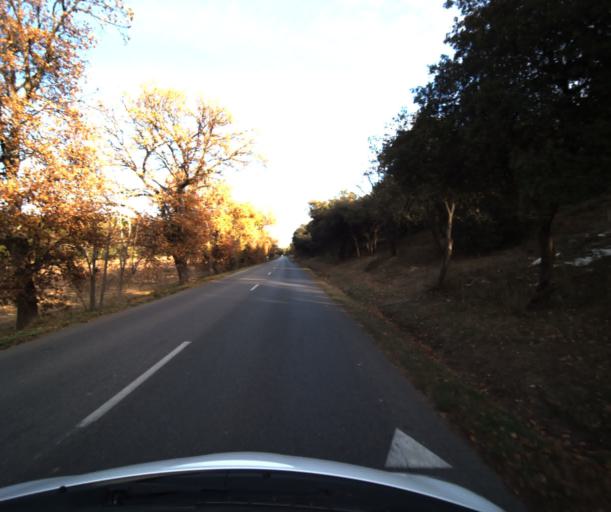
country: FR
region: Provence-Alpes-Cote d'Azur
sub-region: Departement du Vaucluse
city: Pertuis
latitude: 43.6981
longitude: 5.5506
